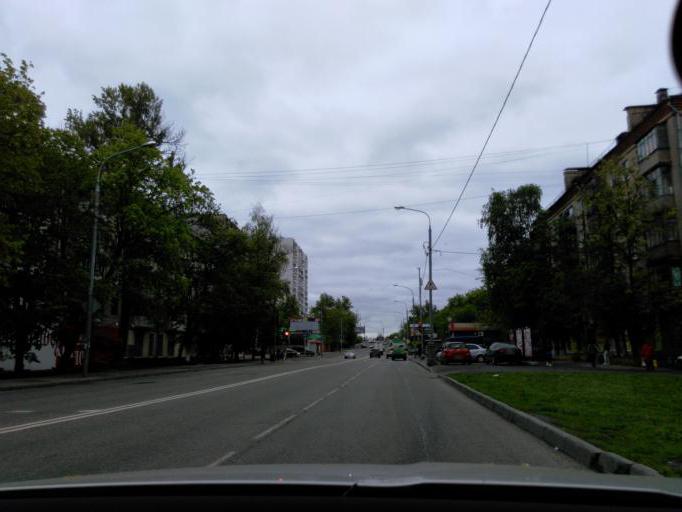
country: RU
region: Moscow
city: Zapadnoye Degunino
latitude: 55.8450
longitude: 37.5215
